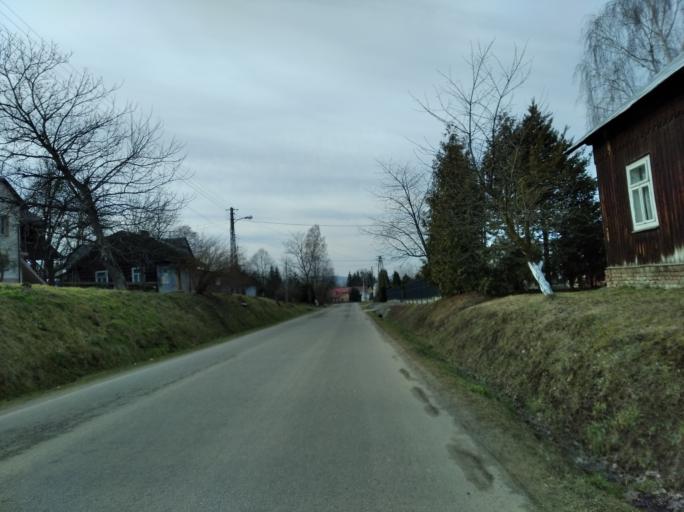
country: PL
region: Subcarpathian Voivodeship
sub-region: Powiat brzozowski
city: Gorki
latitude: 49.6430
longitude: 22.0445
